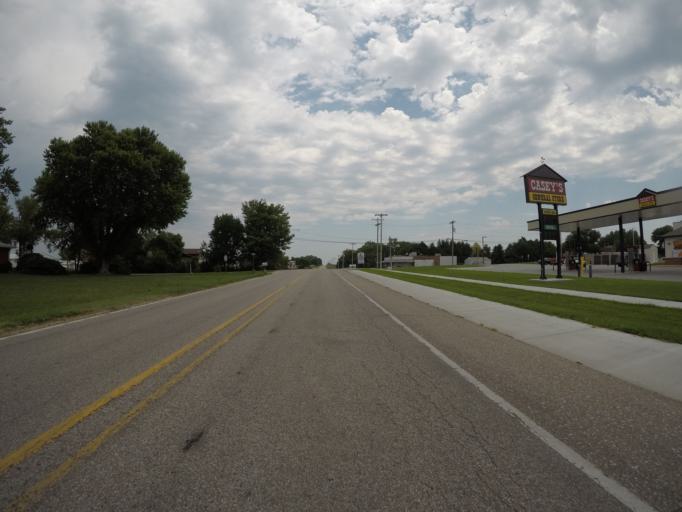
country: US
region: Nebraska
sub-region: Adams County
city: Hastings
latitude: 40.5971
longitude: -98.5072
